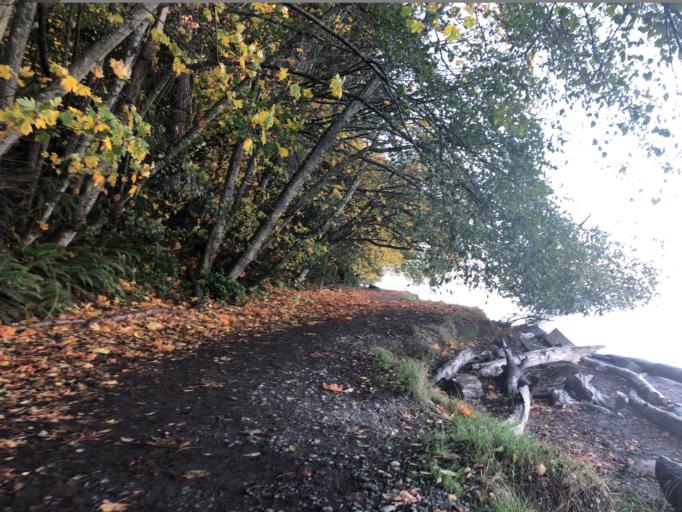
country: US
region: Washington
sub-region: Pierce County
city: Gig Harbor
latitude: 47.3146
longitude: -122.5306
